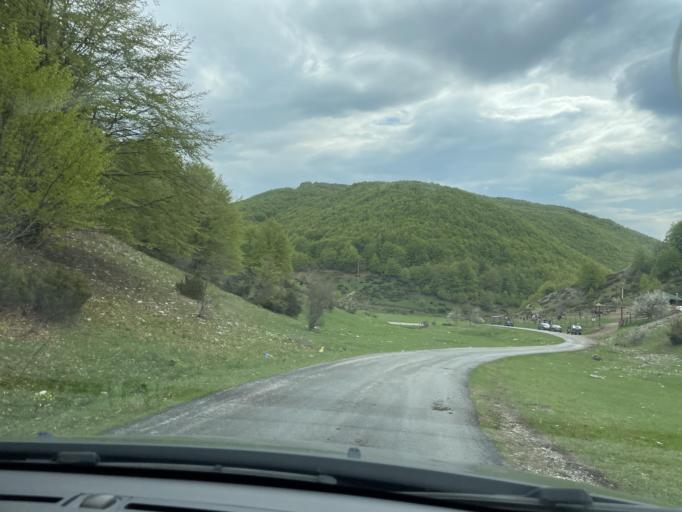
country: MK
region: Opstina Rostusa
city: Rostusha
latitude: 41.5966
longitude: 20.6743
